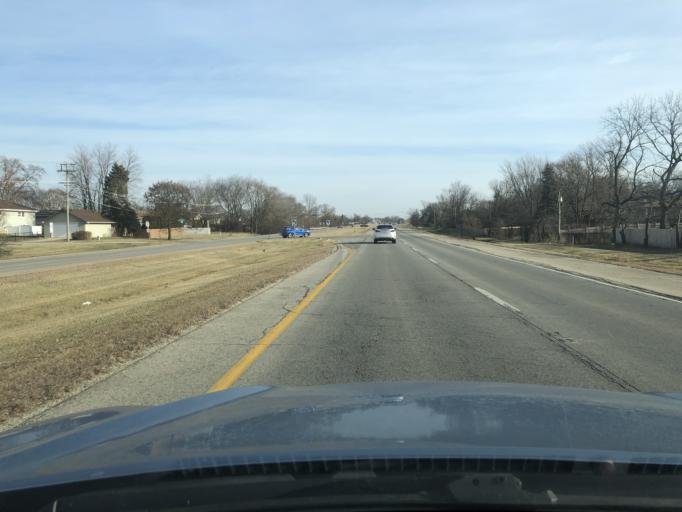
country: US
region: Illinois
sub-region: Cook County
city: South Barrington
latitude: 42.0533
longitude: -88.1179
